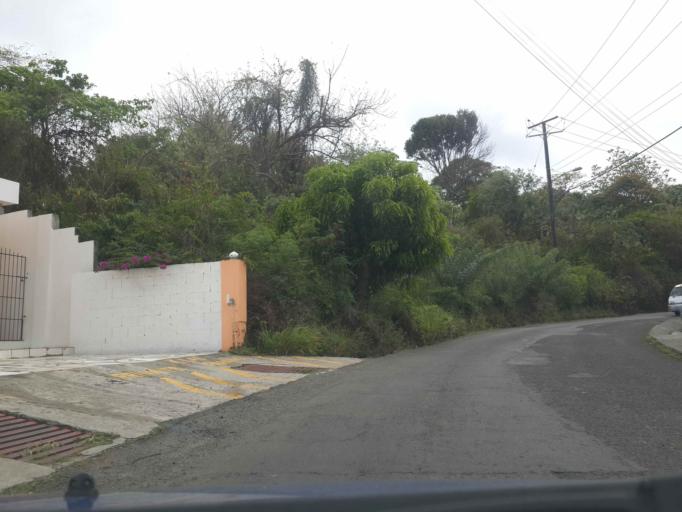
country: LC
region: Castries Quarter
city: Bisee
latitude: 14.0462
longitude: -60.9681
